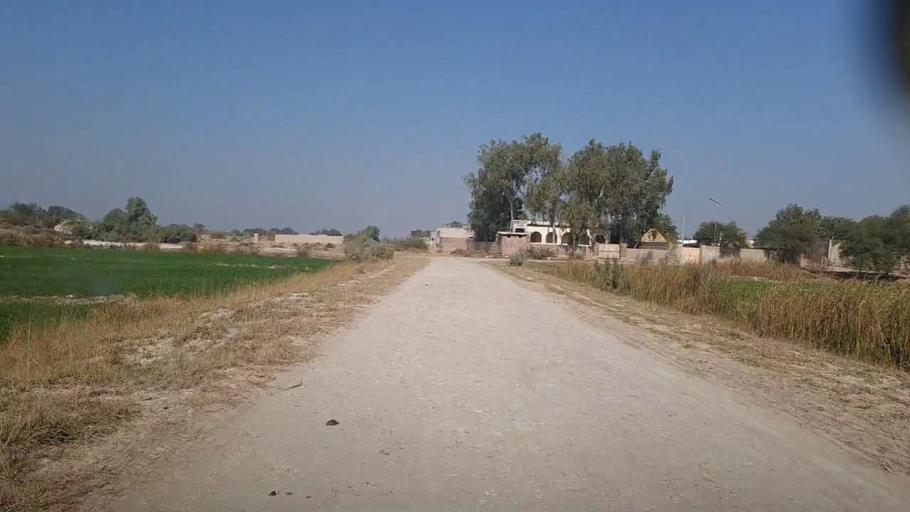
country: PK
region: Sindh
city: Khairpur
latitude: 27.9495
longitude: 69.7284
